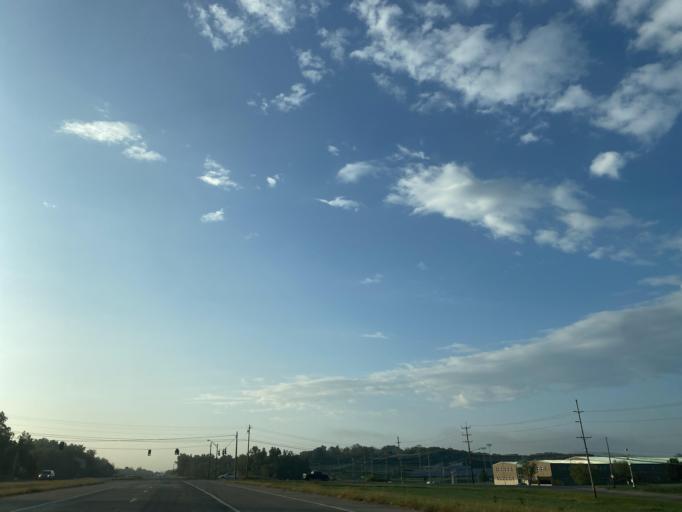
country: US
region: Kentucky
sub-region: Campbell County
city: Claryville
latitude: 38.9223
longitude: -84.3914
